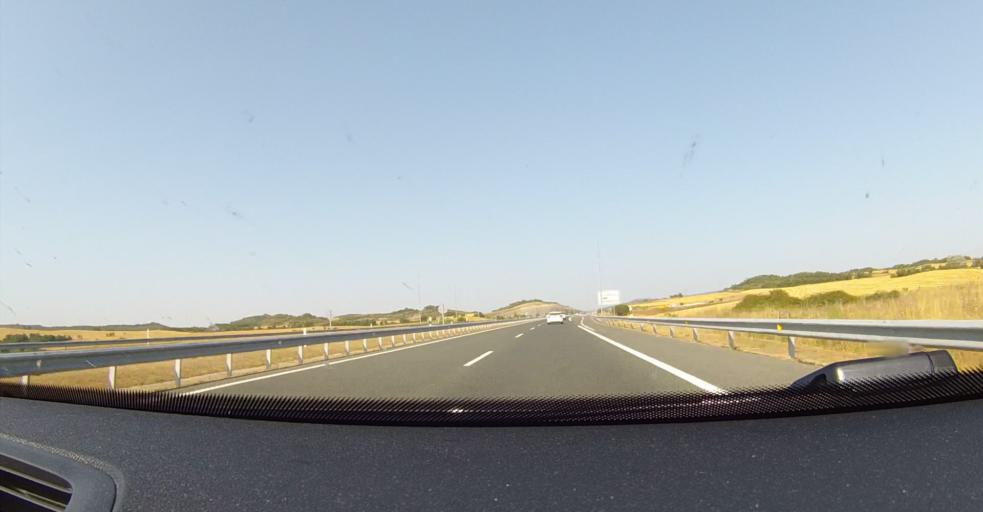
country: ES
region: Basque Country
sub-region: Provincia de Alava
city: Gasteiz / Vitoria
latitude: 42.9197
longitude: -2.6683
